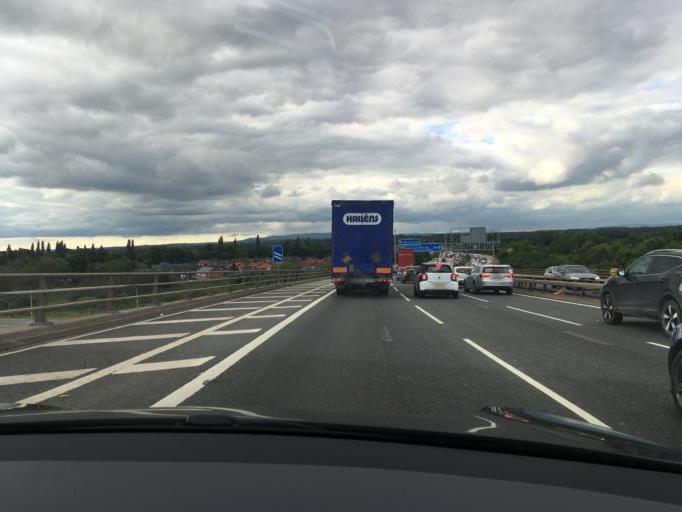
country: GB
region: England
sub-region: Trafford
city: Urmston
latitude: 53.4713
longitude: -2.3714
